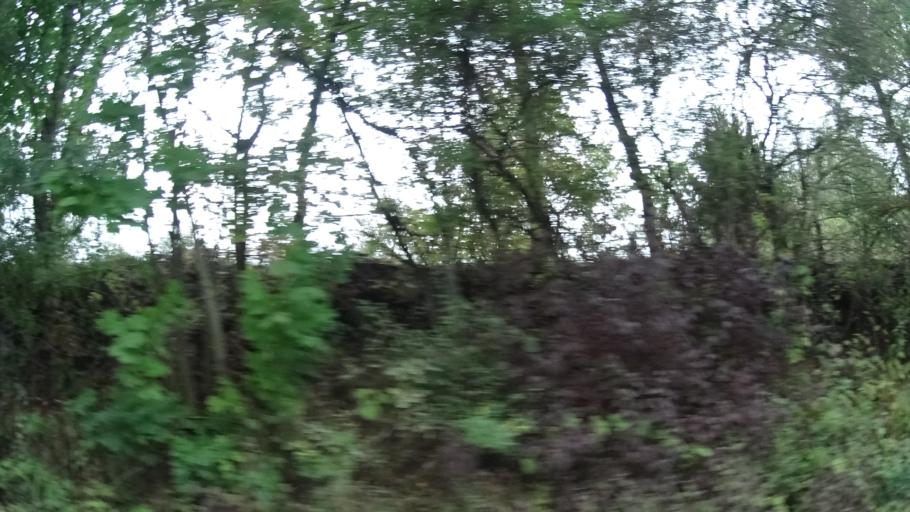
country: DE
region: Hesse
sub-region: Regierungsbezirk Kassel
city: Poppenhausen
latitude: 50.4841
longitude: 9.8099
